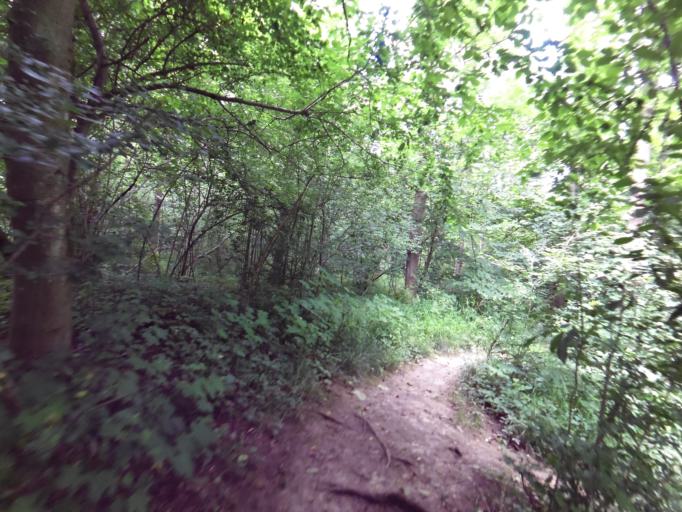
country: CH
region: Zurich
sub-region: Bezirk Zuerich
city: Zuerich (Kreis 10)
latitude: 47.4119
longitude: 8.4993
